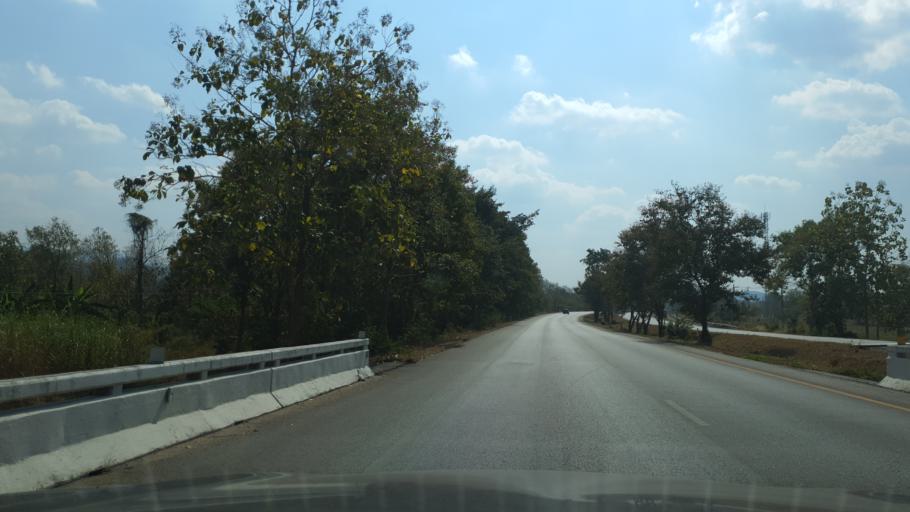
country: TH
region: Lampang
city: Mae Phrik
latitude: 17.4016
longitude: 99.1496
